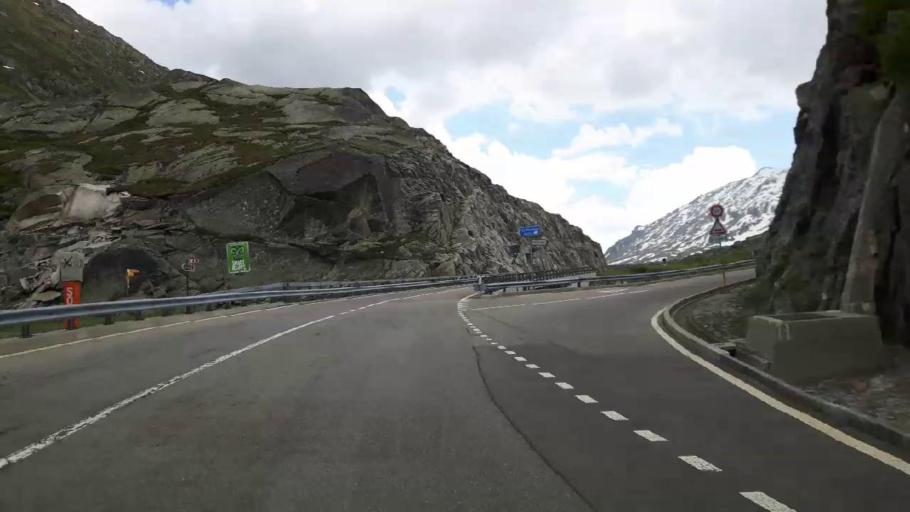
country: CH
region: Uri
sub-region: Uri
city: Andermatt
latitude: 46.5821
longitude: 8.5590
